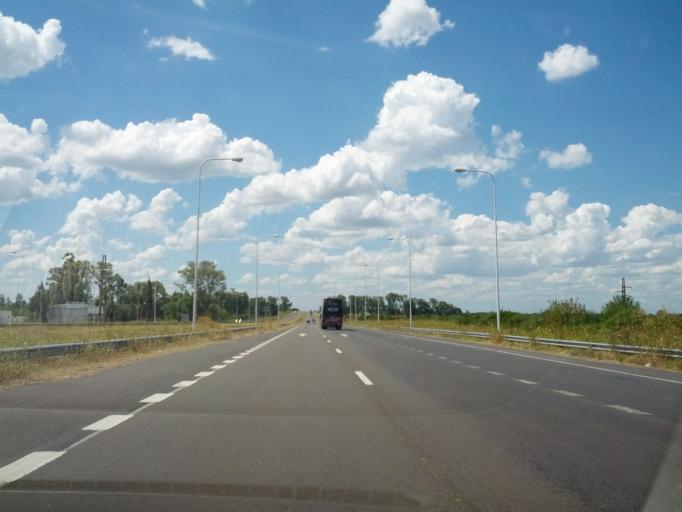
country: AR
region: Entre Rios
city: Concepcion del Uruguay
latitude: -32.4743
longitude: -58.3038
